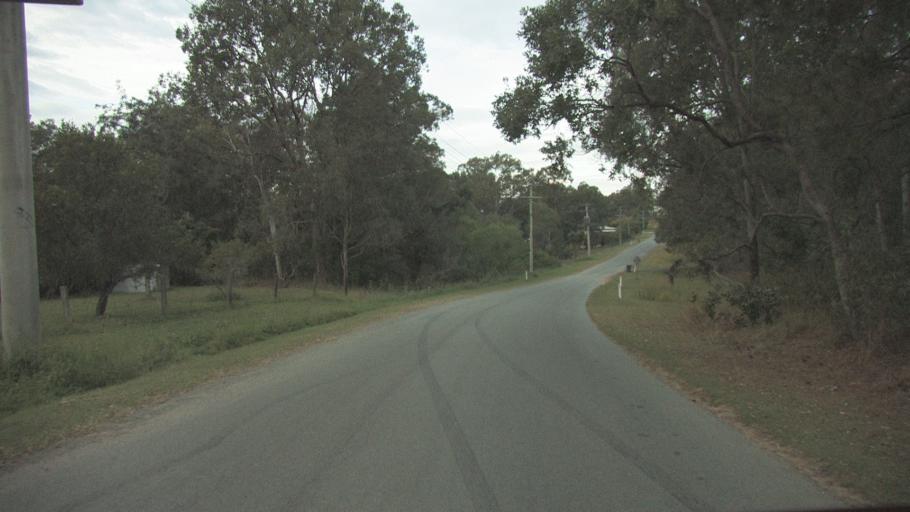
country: AU
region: Queensland
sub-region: Logan
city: Chambers Flat
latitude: -27.8204
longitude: 153.0920
